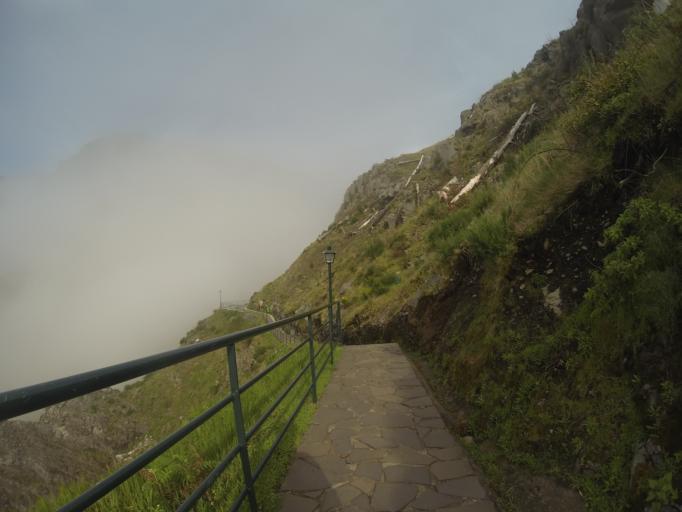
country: PT
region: Madeira
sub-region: Camara de Lobos
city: Curral das Freiras
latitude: 32.7103
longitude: -16.9648
